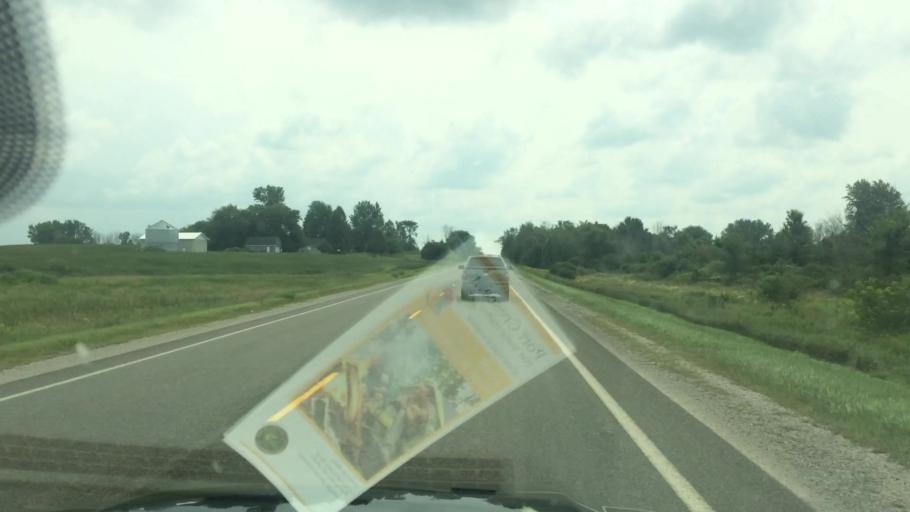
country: US
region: Michigan
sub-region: Tuscola County
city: Cass City
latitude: 43.6836
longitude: -83.0982
